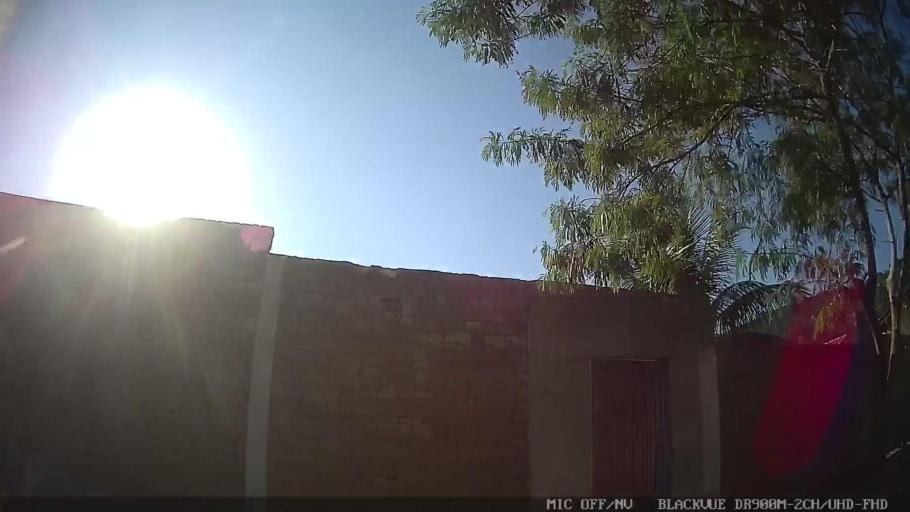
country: BR
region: Sao Paulo
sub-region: Guaruja
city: Guaruja
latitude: -24.0151
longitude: -46.2871
